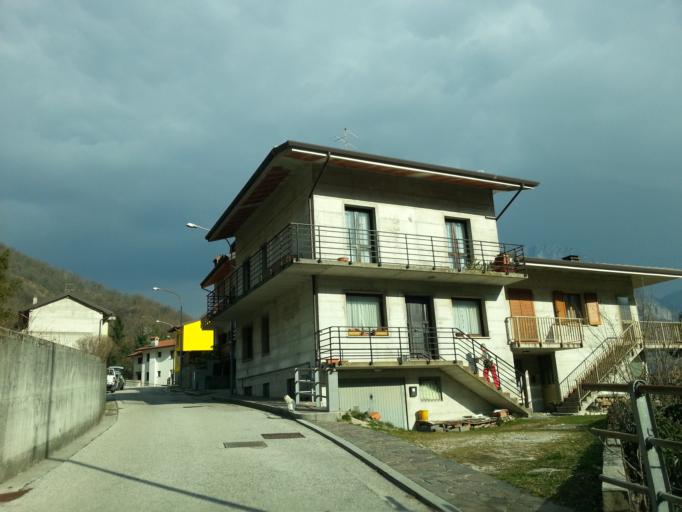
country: IT
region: Friuli Venezia Giulia
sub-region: Provincia di Udine
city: Bordano
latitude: 46.3167
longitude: 13.1018
